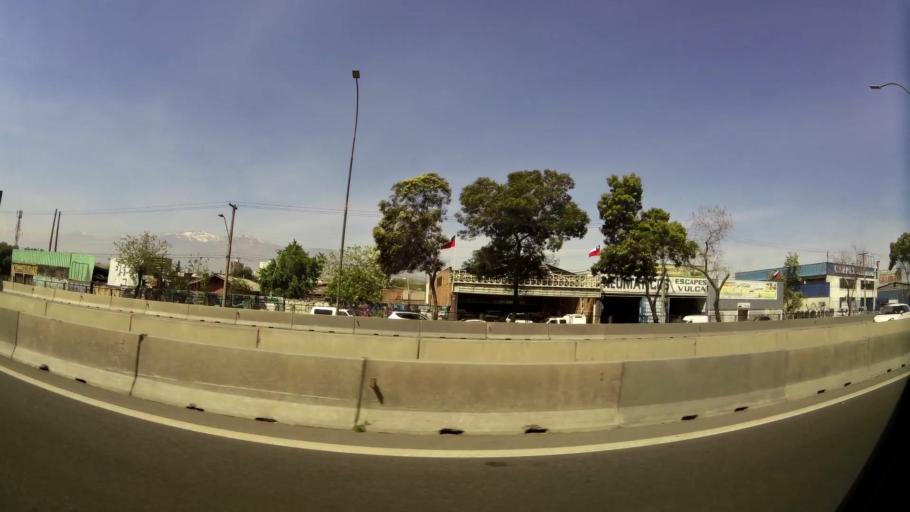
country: CL
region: Santiago Metropolitan
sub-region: Provincia de Santiago
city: Santiago
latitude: -33.5037
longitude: -70.6678
